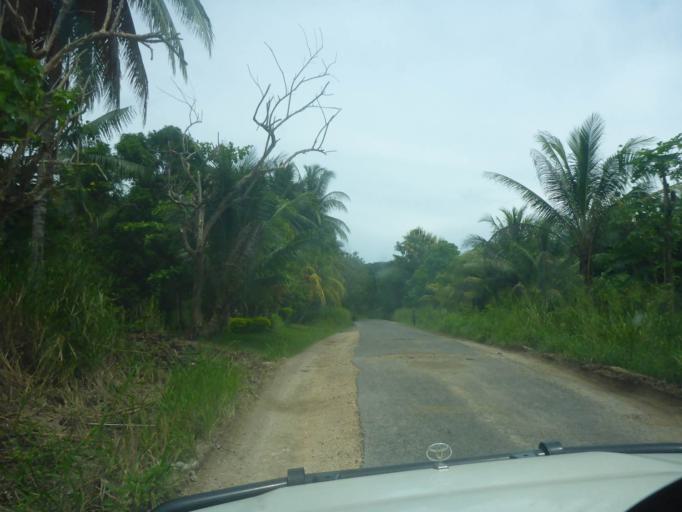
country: PG
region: Madang
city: Madang
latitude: -4.6531
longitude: 145.5799
